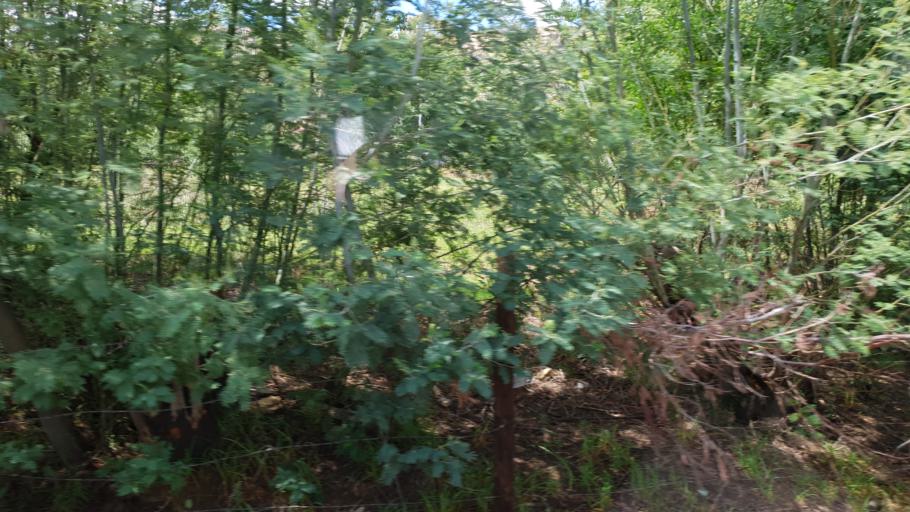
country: LS
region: Maseru
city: Nako
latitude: -29.6299
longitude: 27.5040
